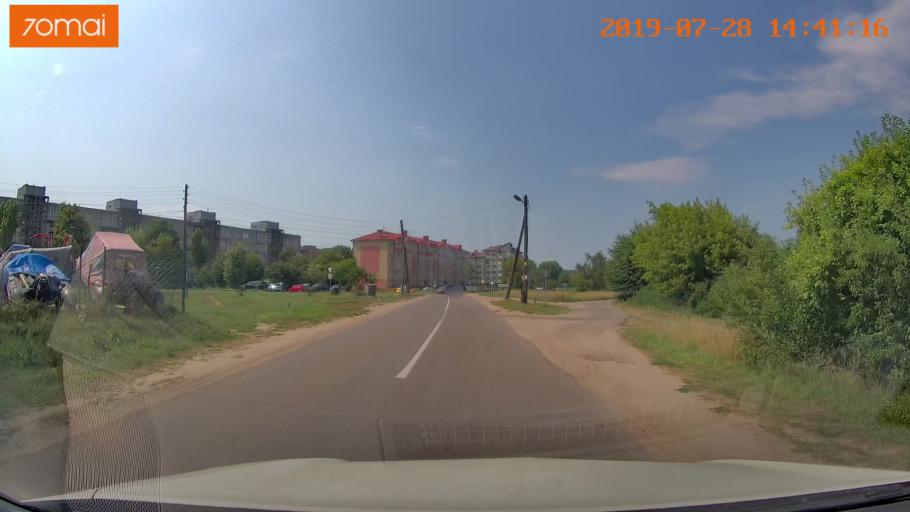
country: RU
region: Kaliningrad
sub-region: Gorod Kaliningrad
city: Yantarnyy
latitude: 54.8556
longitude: 19.9496
